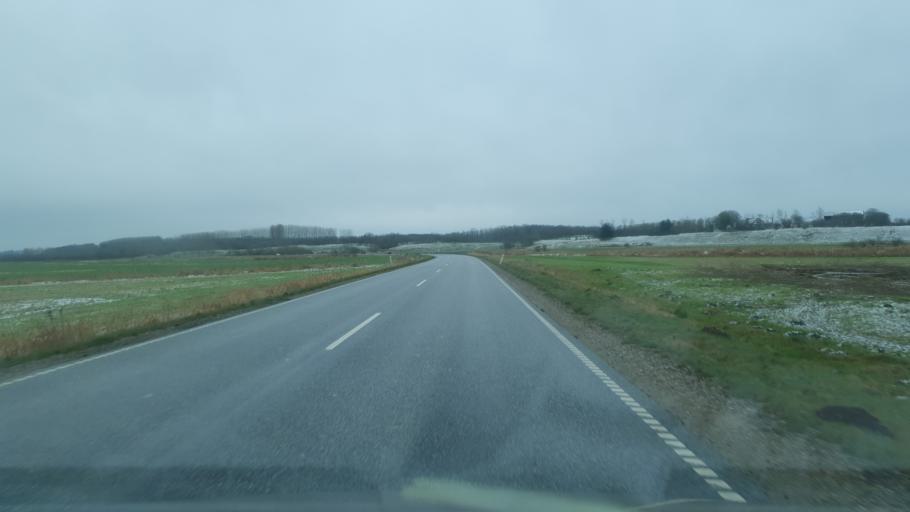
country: DK
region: North Denmark
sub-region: Vesthimmerland Kommune
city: Logstor
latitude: 56.9640
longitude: 9.4051
